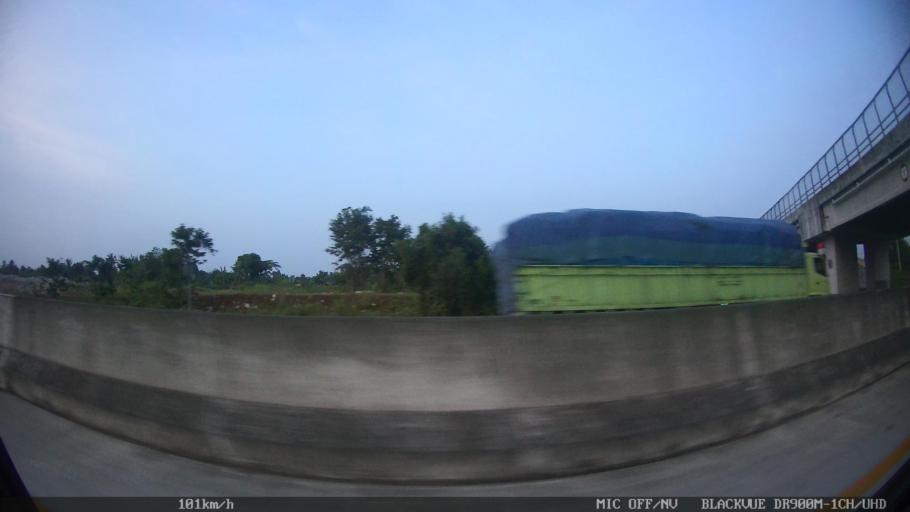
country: ID
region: Lampung
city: Kalianda
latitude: -5.6879
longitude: 105.6175
